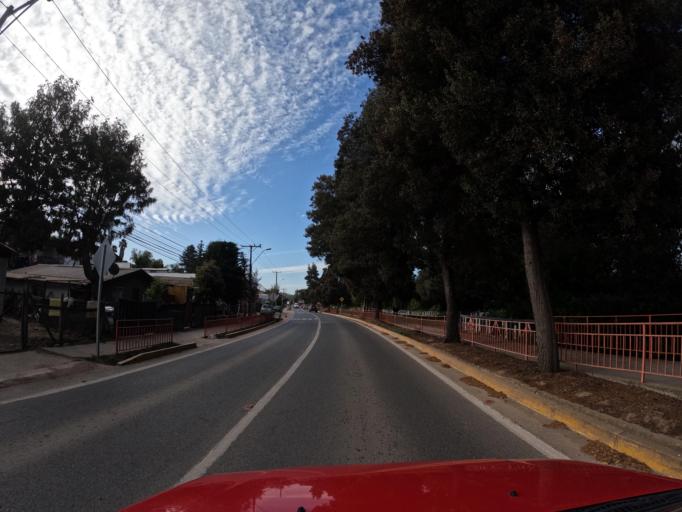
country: CL
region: Valparaiso
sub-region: San Antonio Province
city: San Antonio
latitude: -34.1240
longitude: -71.7265
